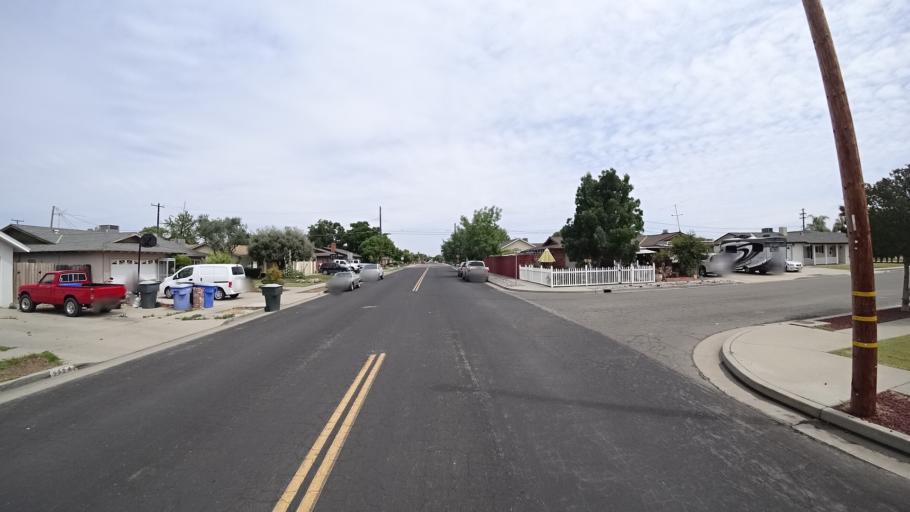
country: US
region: California
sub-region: Kings County
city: Hanford
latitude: 36.3546
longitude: -119.6397
